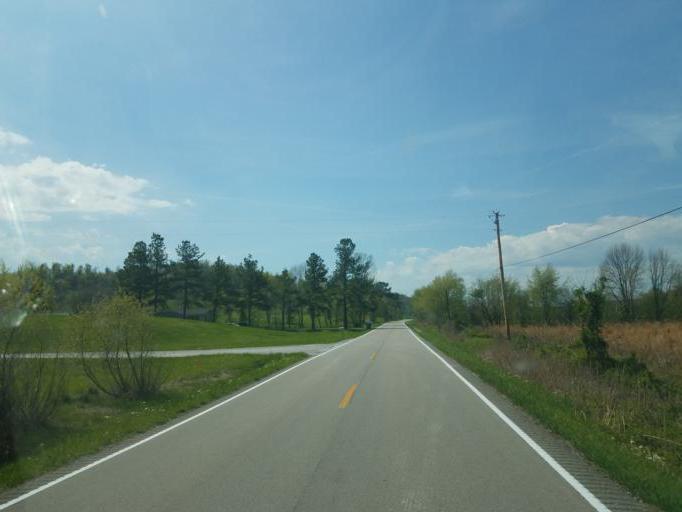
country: US
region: Kentucky
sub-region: Edmonson County
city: Brownsville
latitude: 37.3018
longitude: -86.4314
